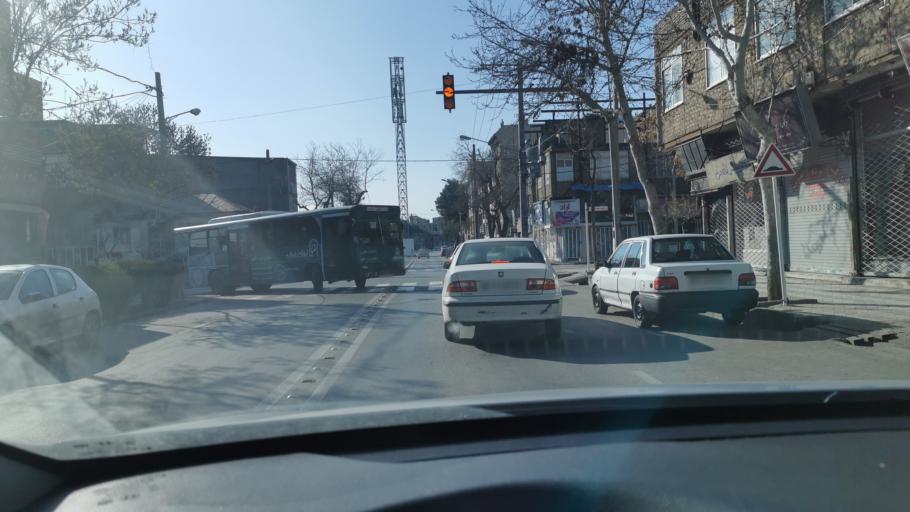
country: IR
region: Razavi Khorasan
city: Mashhad
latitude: 36.2768
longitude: 59.5755
